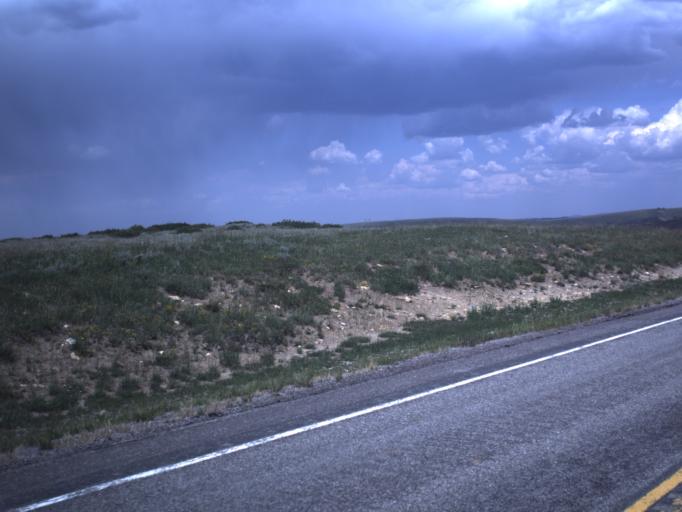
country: US
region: Utah
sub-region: Sanpete County
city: Fairview
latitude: 39.6169
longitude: -111.3008
